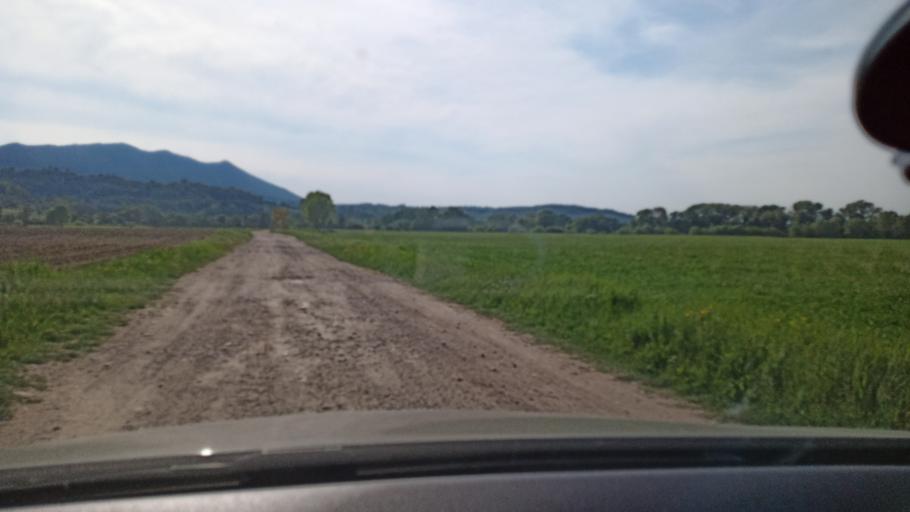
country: IT
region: Latium
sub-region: Citta metropolitana di Roma Capitale
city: Ponzano Romano
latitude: 42.2704
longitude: 12.5700
